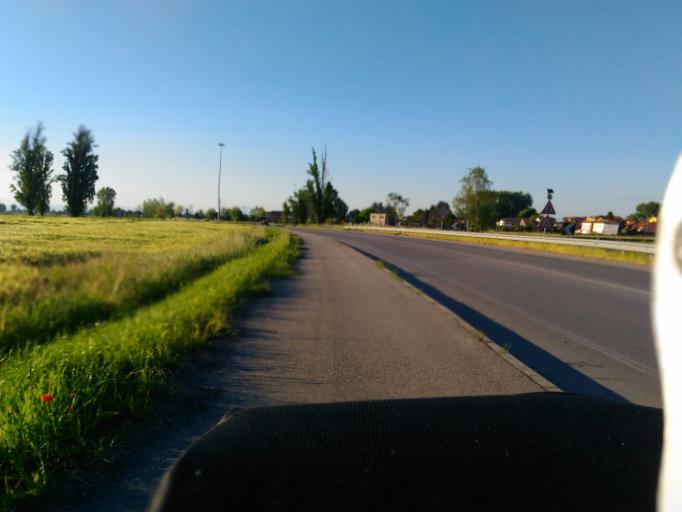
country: IT
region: Lombardy
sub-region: Provincia di Lodi
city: Lodi
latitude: 45.3328
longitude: 9.5180
